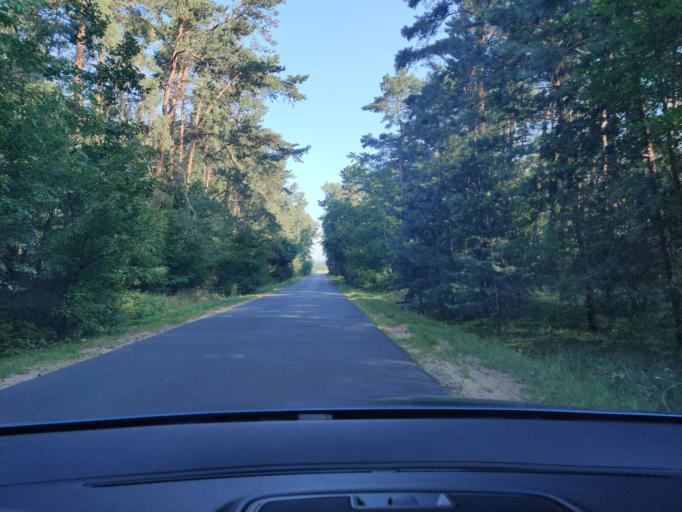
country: PL
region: Greater Poland Voivodeship
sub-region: Konin
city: Konin
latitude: 52.1816
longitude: 18.3332
